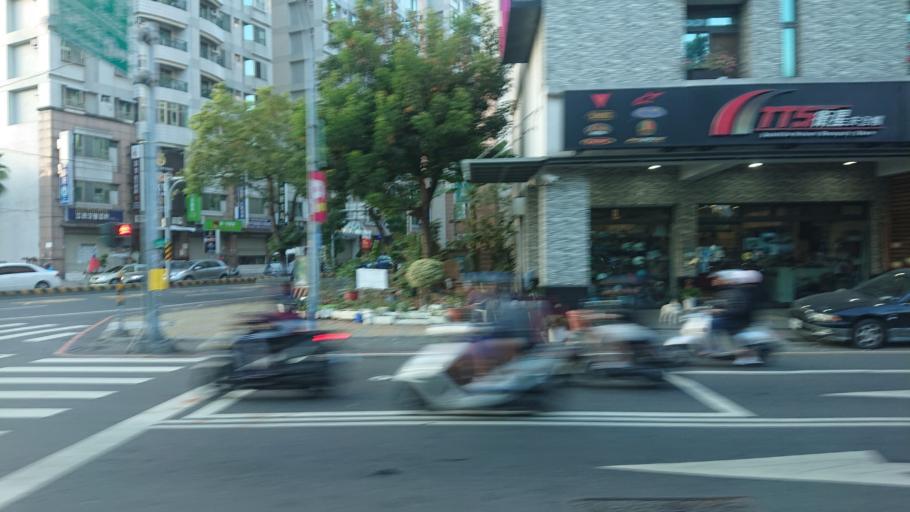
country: TW
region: Taiwan
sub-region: Tainan
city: Tainan
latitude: 23.0080
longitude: 120.2211
